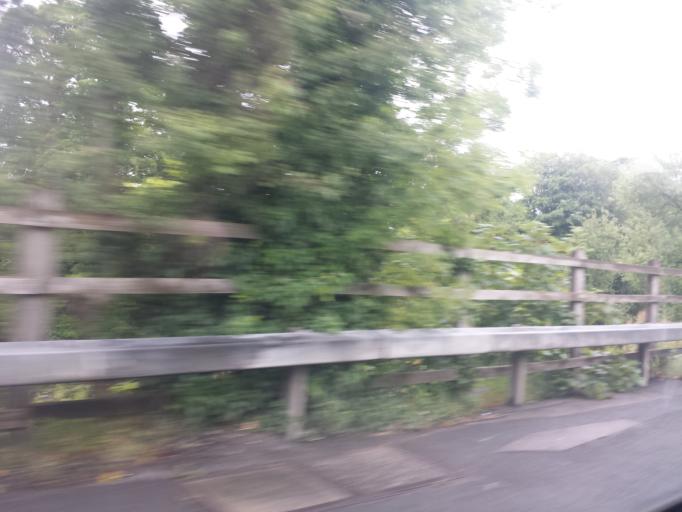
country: GB
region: England
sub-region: Bradford
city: Ilkley
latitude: 53.9292
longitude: -1.7953
